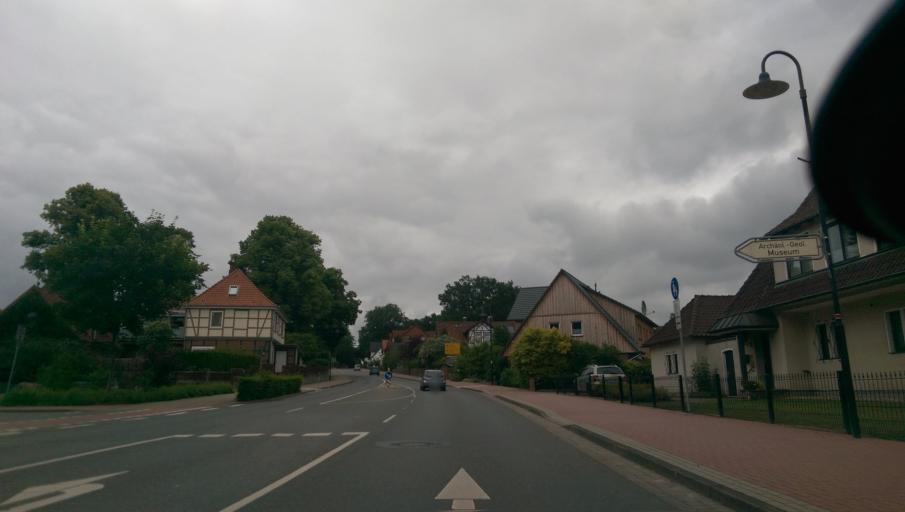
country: DE
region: Lower Saxony
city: Bad Fallingbostel
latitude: 52.8673
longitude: 9.6959
